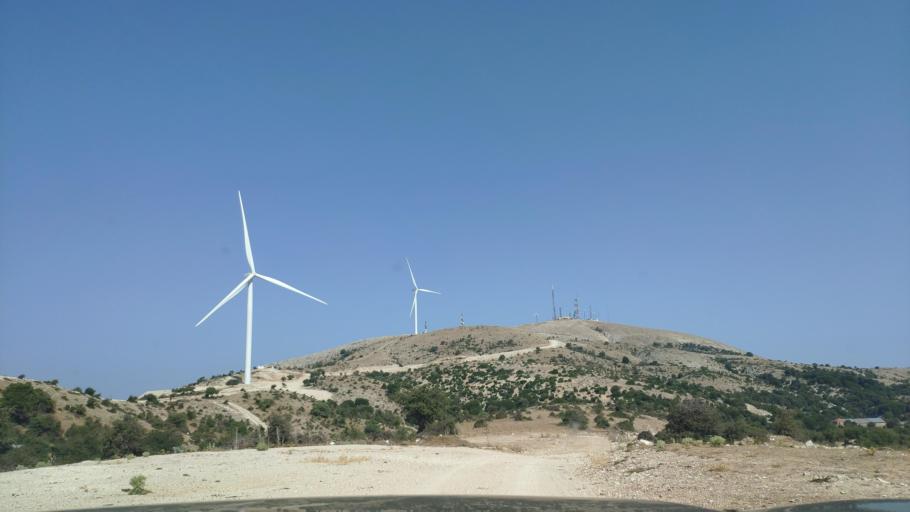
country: GR
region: West Greece
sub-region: Nomos Aitolias kai Akarnanias
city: Monastirakion
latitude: 38.7966
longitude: 20.9988
